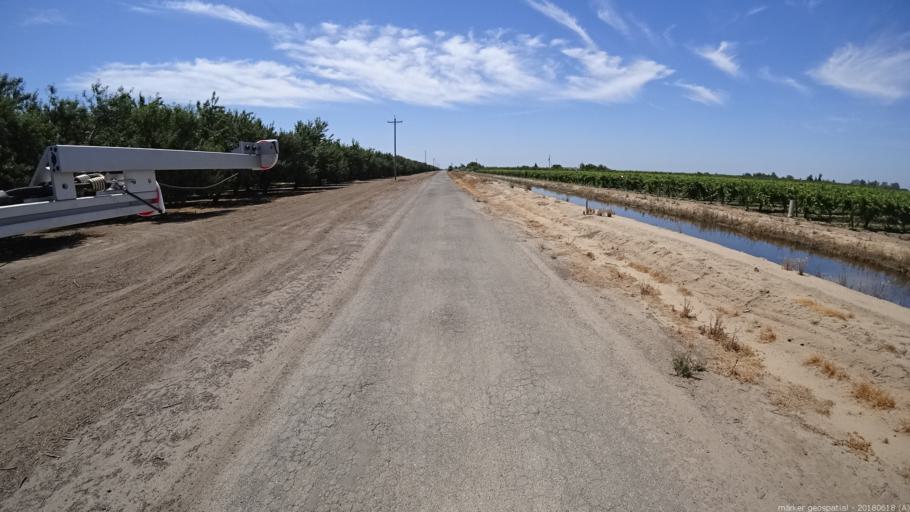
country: US
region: California
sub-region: Madera County
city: Parkwood
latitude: 36.8878
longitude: -120.1014
